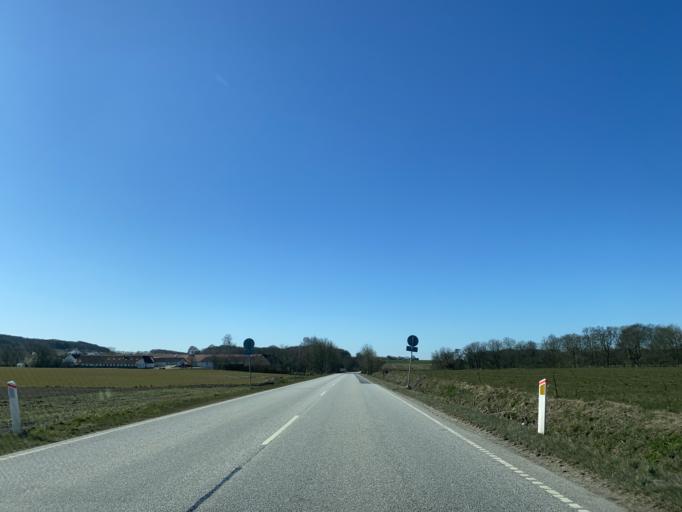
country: DK
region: Central Jutland
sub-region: Randers Kommune
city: Randers
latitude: 56.3991
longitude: 9.9867
